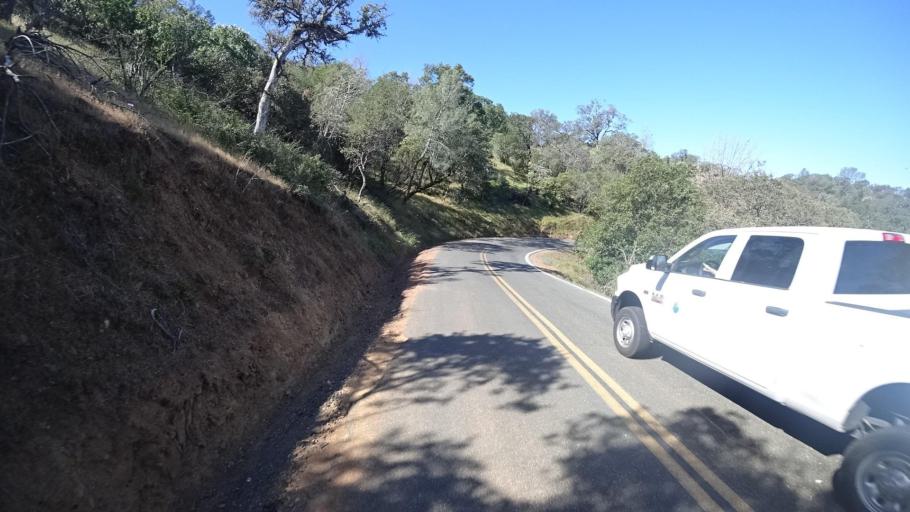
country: US
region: California
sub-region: Lake County
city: Clearlake Oaks
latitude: 39.0029
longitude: -122.7069
